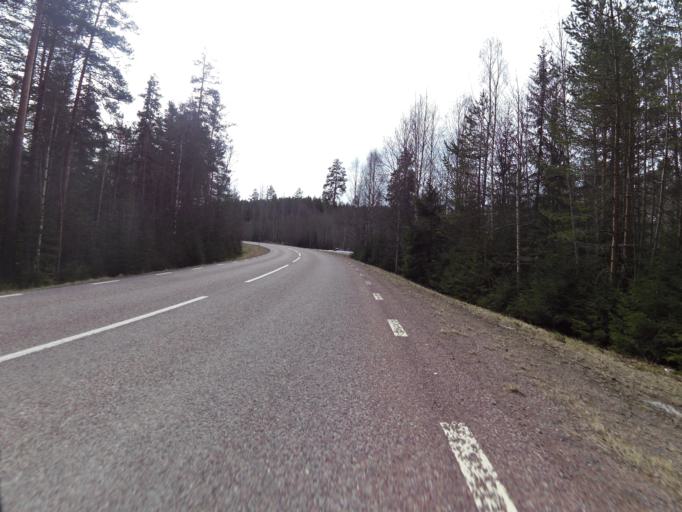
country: SE
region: Dalarna
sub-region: Hedemora Kommun
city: Langshyttan
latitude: 60.5445
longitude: 16.1232
